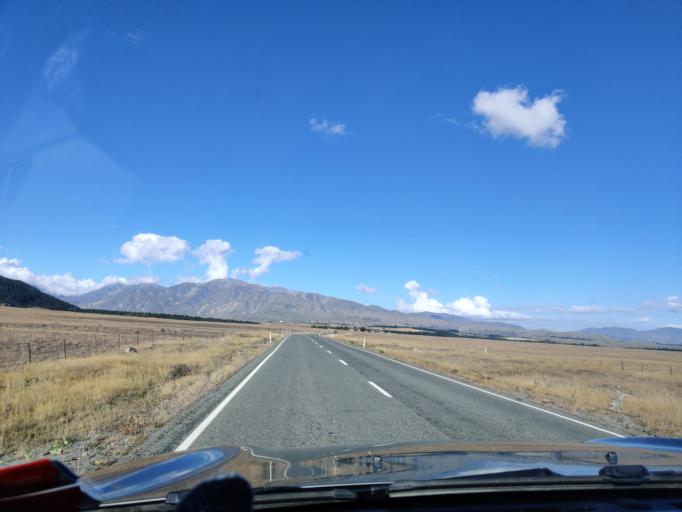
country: NZ
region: Canterbury
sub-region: Timaru District
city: Pleasant Point
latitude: -43.9980
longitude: 170.4264
